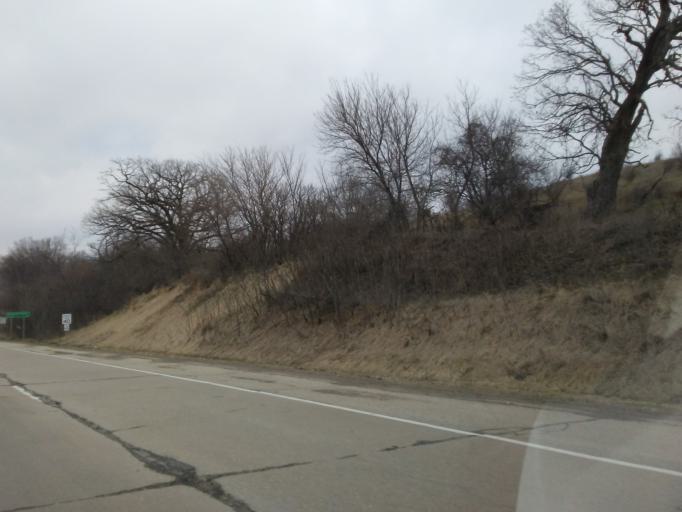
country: US
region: Wisconsin
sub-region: Richland County
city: Richland Center
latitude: 43.3168
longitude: -90.3553
